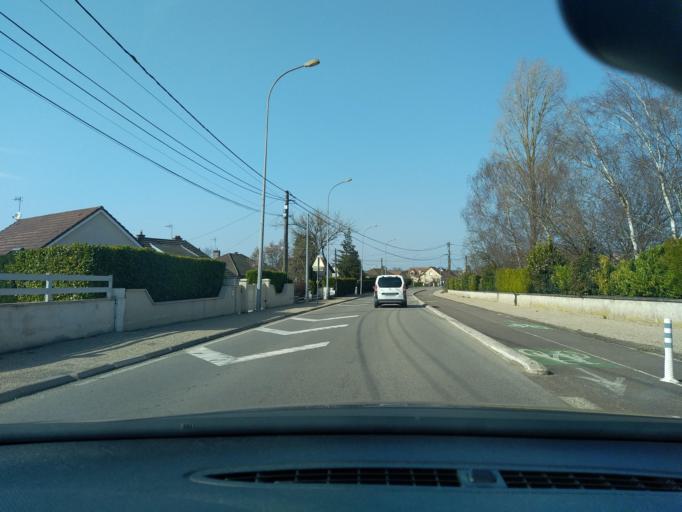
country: FR
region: Franche-Comte
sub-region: Departement du Jura
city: Dole
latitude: 47.0723
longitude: 5.5026
